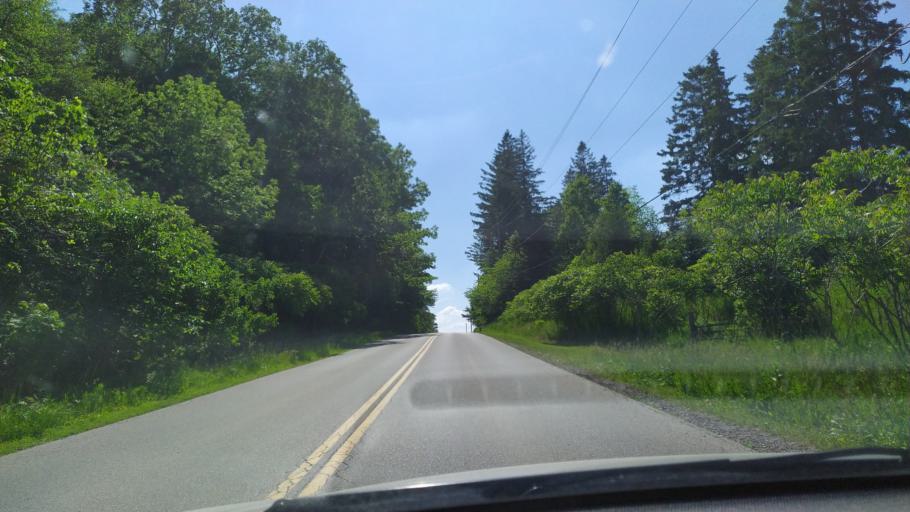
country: CA
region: Ontario
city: Kitchener
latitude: 43.3685
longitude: -80.5757
